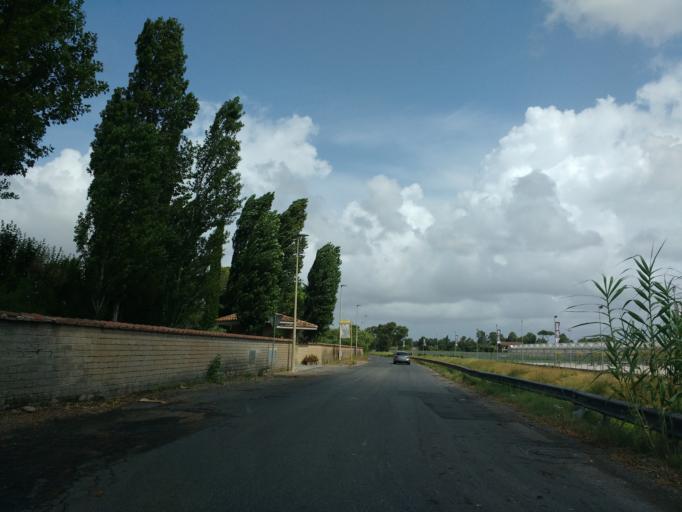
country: IT
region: Latium
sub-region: Citta metropolitana di Roma Capitale
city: Acilia-Castel Fusano-Ostia Antica
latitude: 41.7610
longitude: 12.3291
